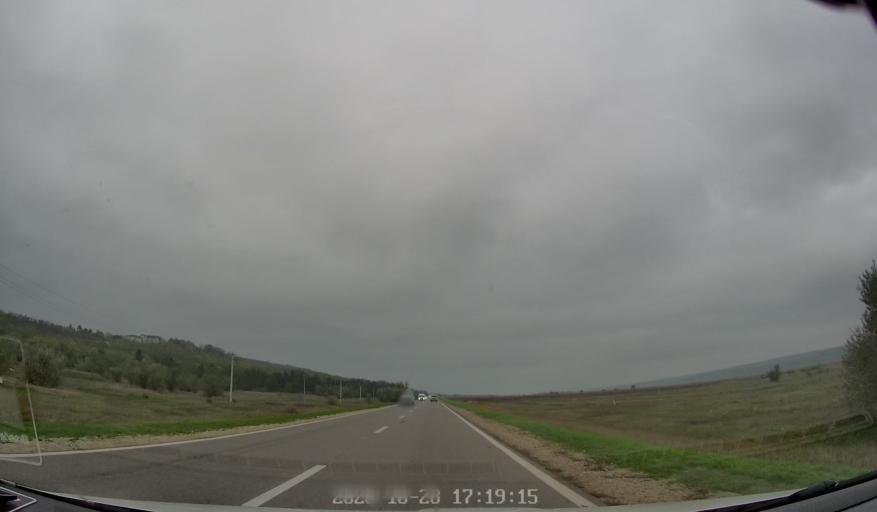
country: MD
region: Cimislia
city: Cimislia
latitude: 46.5561
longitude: 28.7668
